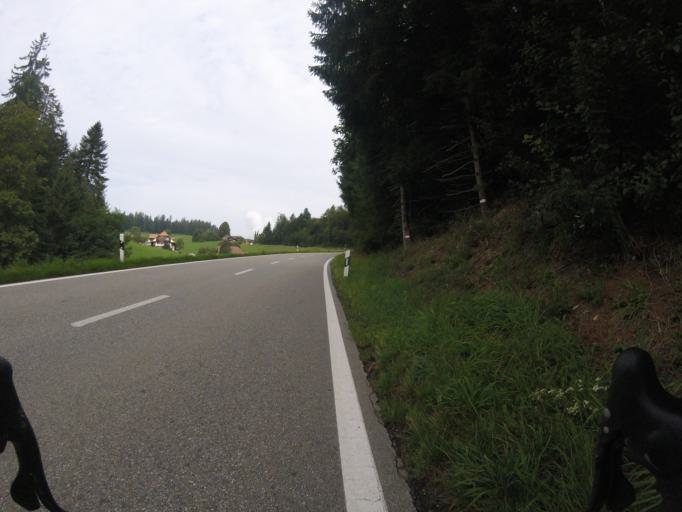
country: CH
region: Bern
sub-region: Bern-Mittelland District
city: Walkringen
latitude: 46.9447
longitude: 7.6510
